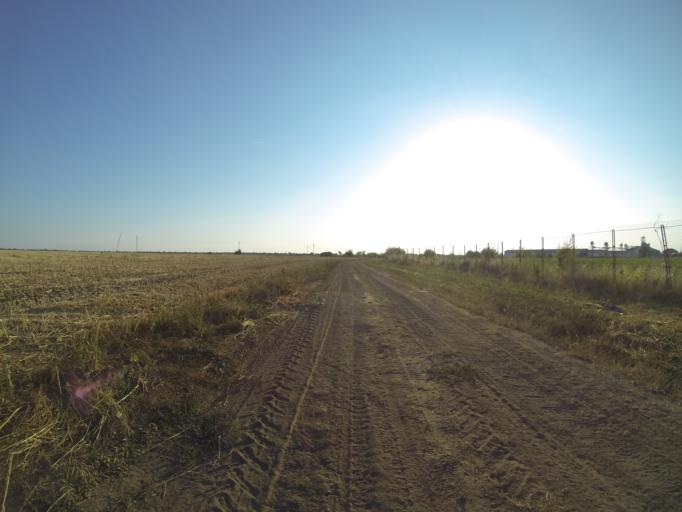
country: RO
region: Dolj
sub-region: Comuna Giurgita
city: Giurgita
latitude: 44.0308
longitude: 23.6463
